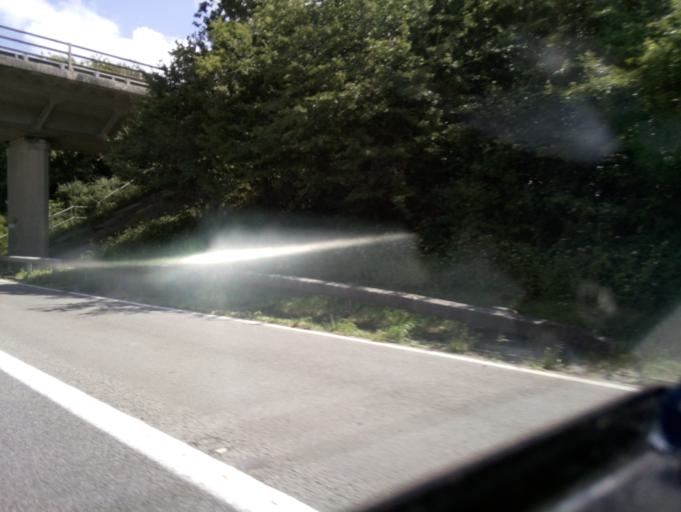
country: GB
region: England
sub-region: Wiltshire
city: Lyneham
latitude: 51.5462
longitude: -1.9646
